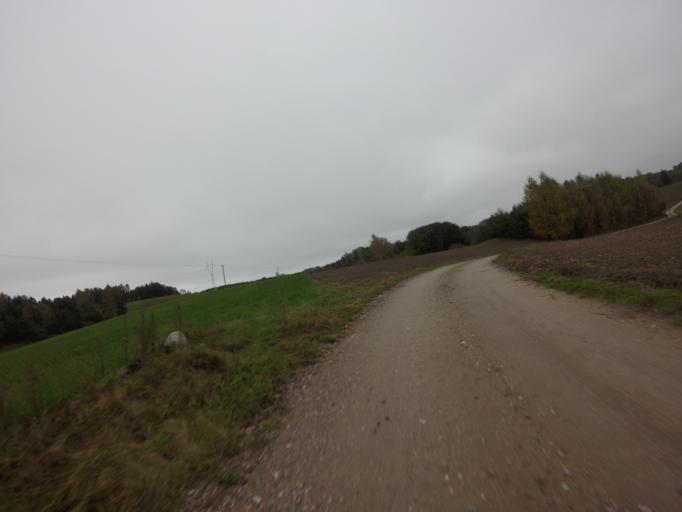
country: PL
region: Pomeranian Voivodeship
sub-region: Powiat kartuski
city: Stezyca
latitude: 54.1747
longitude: 17.9497
